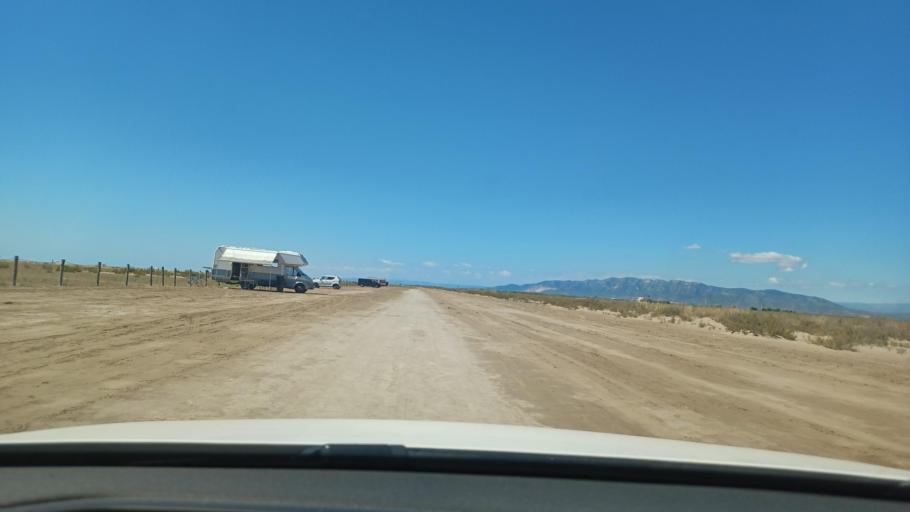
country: ES
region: Catalonia
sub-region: Provincia de Tarragona
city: Deltebre
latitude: 40.6496
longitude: 0.7733
